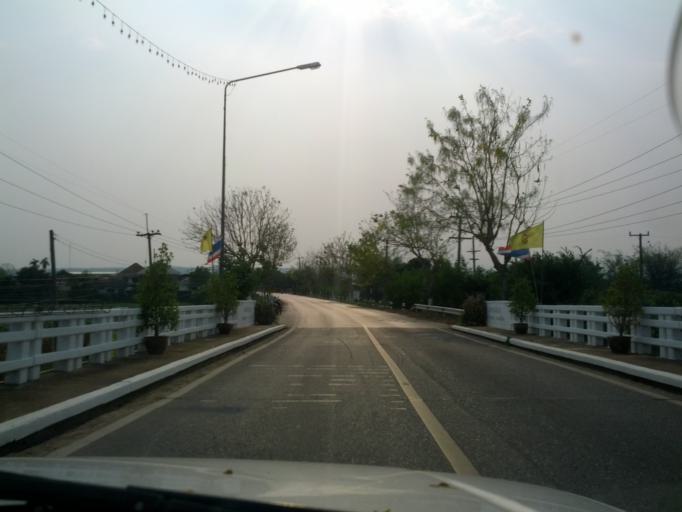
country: TH
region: Chiang Mai
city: Mae Taeng
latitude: 19.1460
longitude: 99.0061
